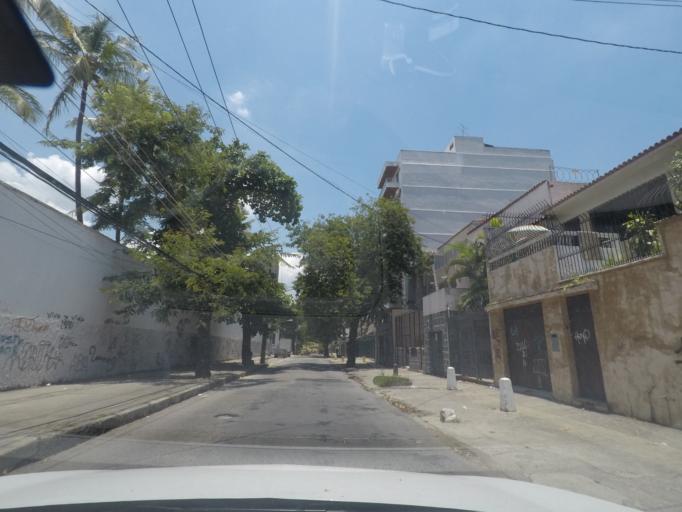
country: BR
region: Rio de Janeiro
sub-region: Rio De Janeiro
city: Rio de Janeiro
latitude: -22.9212
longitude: -43.2489
